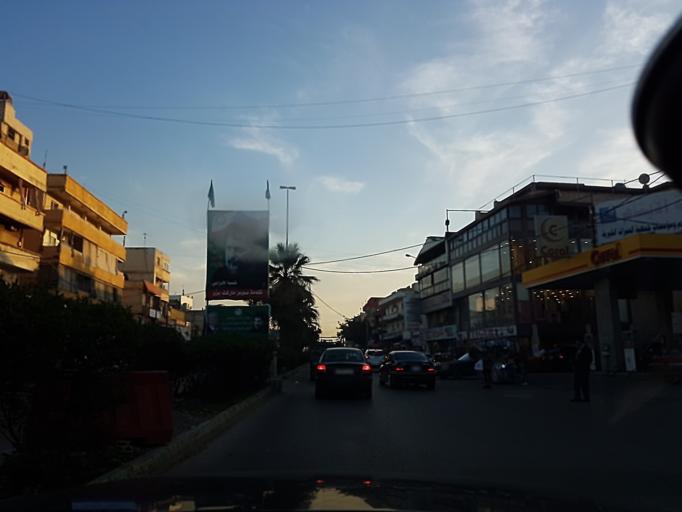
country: LB
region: Beyrouth
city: Beirut
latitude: 33.8494
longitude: 35.4852
